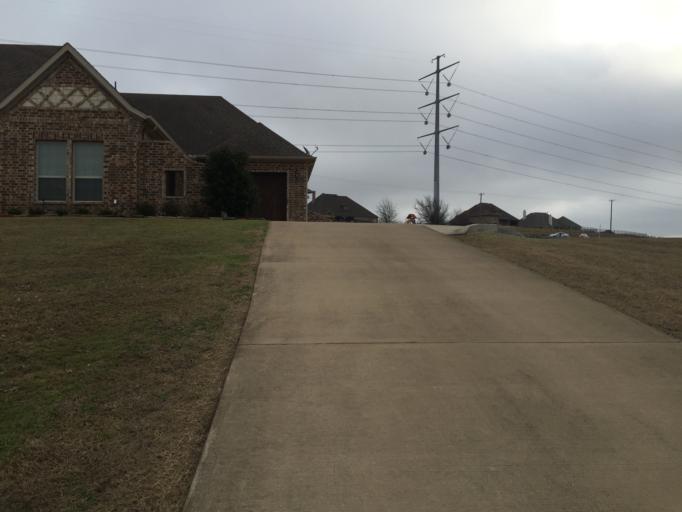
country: US
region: Texas
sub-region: Tarrant County
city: Benbrook
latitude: 32.6321
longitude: -97.5347
